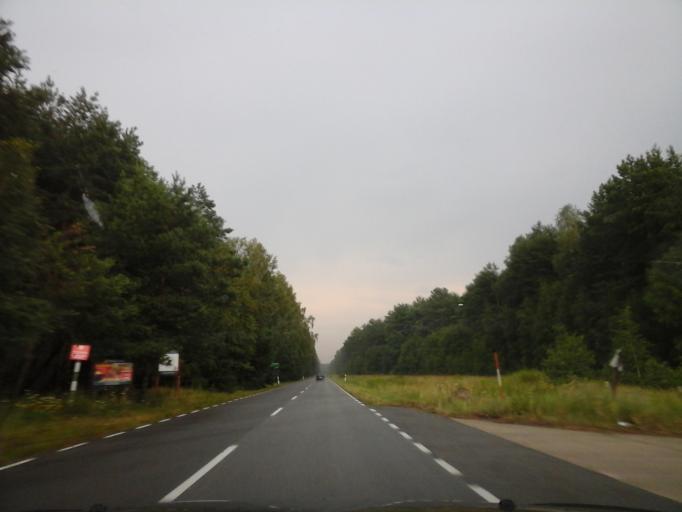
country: PL
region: Greater Poland Voivodeship
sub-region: Powiat miedzychodzki
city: Miedzychod
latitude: 52.5011
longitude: 15.9263
